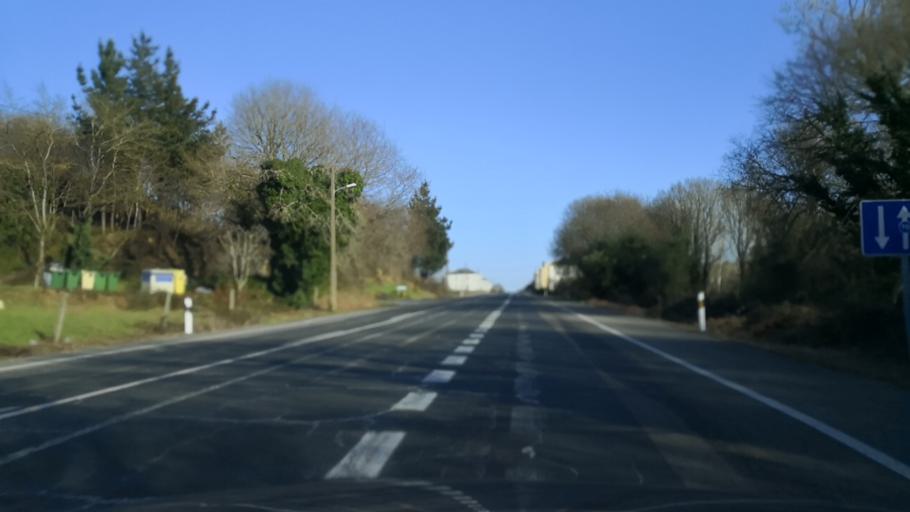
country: ES
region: Galicia
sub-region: Provincia de Lugo
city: Corgo
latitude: 42.9598
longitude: -7.4759
